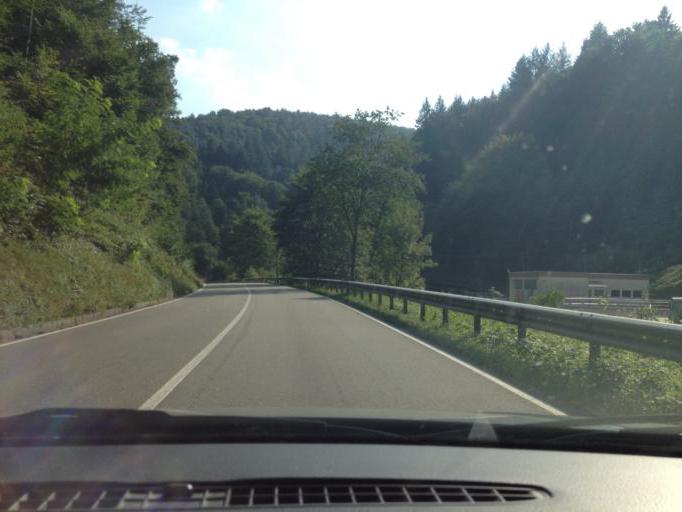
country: DE
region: Rheinland-Pfalz
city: Weidenthal
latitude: 49.4112
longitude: 8.0070
